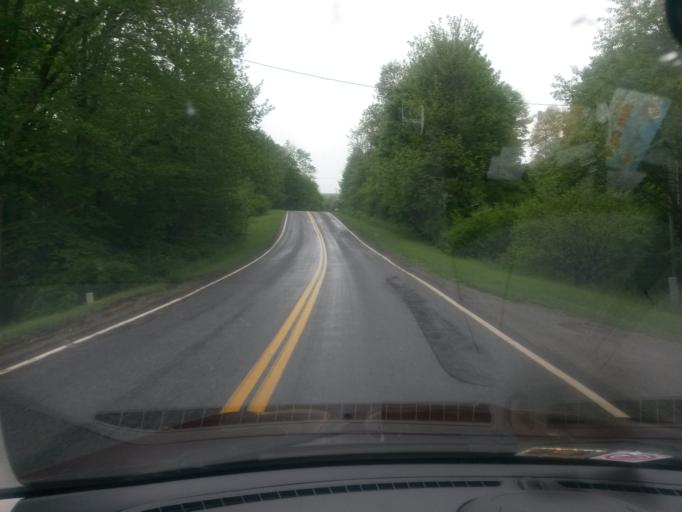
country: US
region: Virginia
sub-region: Floyd County
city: Floyd
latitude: 36.7679
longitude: -80.3874
